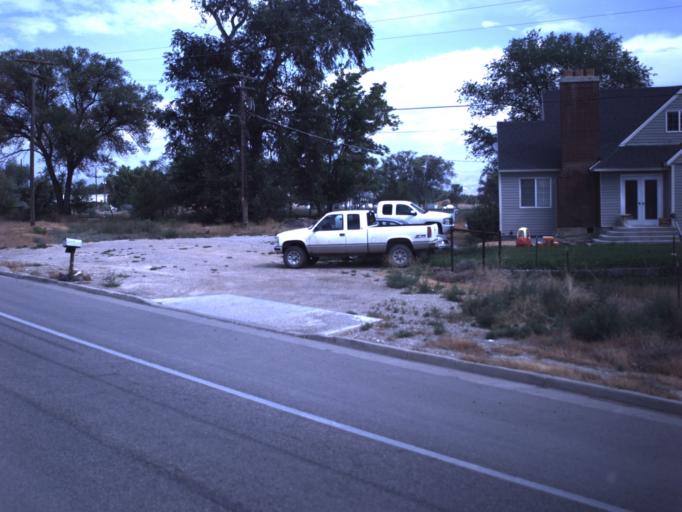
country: US
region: Utah
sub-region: Uintah County
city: Naples
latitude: 40.4138
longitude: -109.4975
